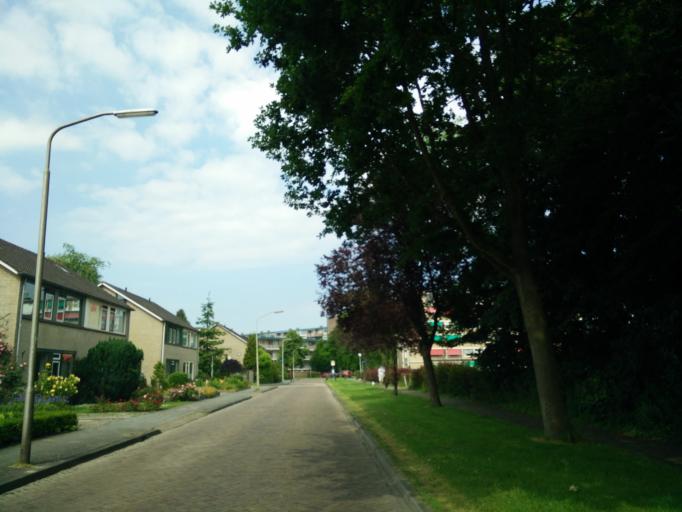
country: NL
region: Drenthe
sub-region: Gemeente Assen
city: Assen
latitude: 52.9964
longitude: 6.5418
